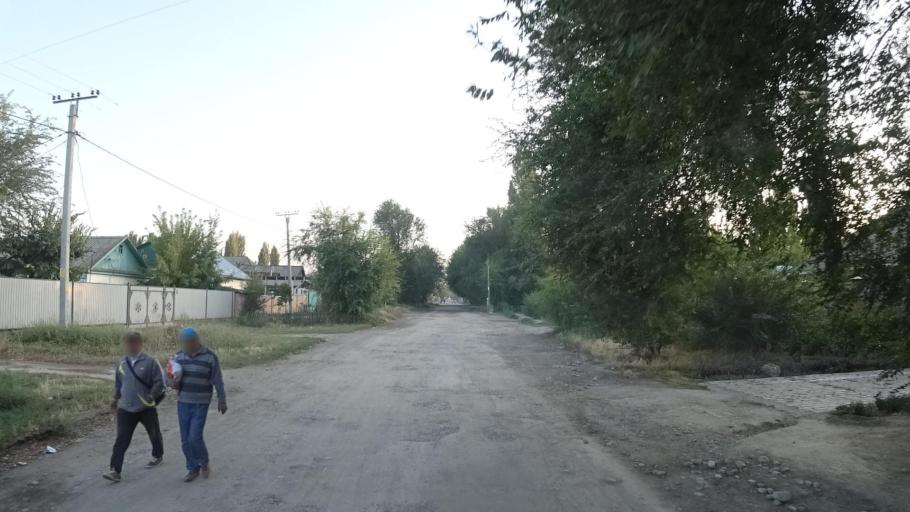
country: KG
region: Chuy
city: Lebedinovka
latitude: 42.8774
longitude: 74.7199
